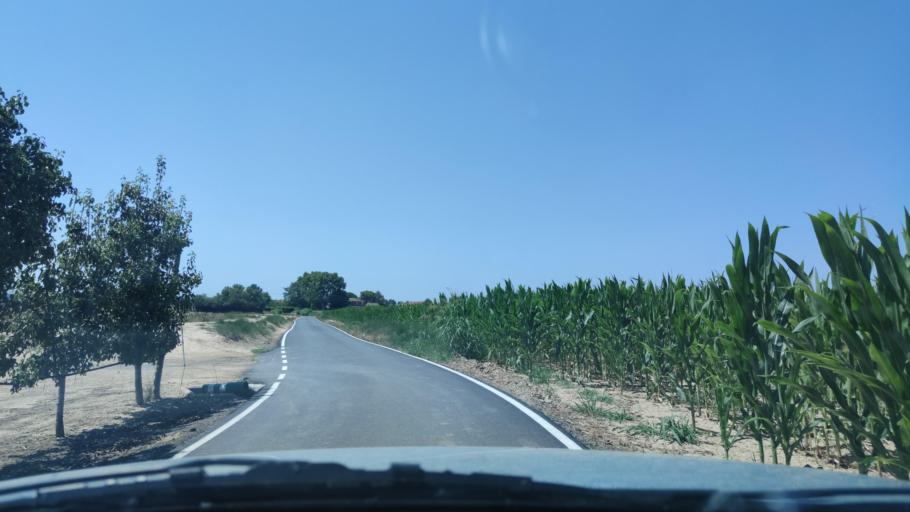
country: ES
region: Catalonia
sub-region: Provincia de Lleida
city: Alpicat
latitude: 41.6556
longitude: 0.5677
